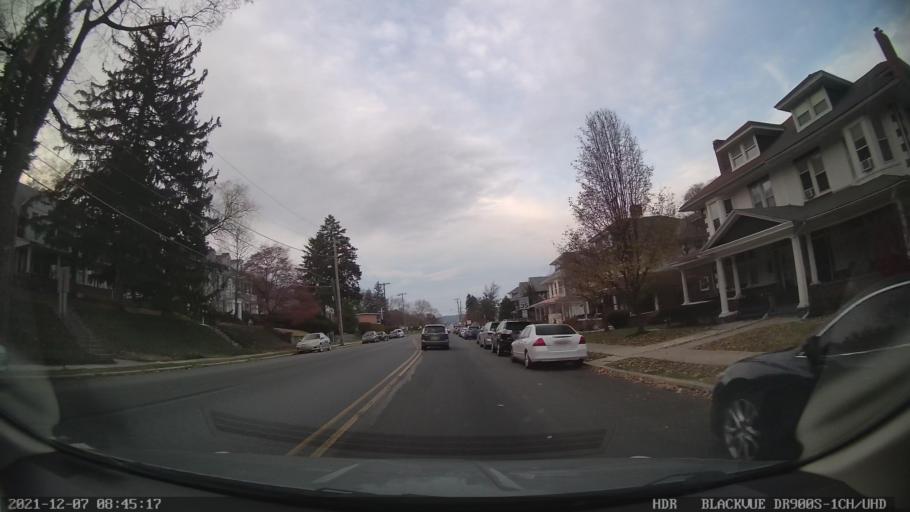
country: US
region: Pennsylvania
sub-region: Berks County
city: Hyde Park
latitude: 40.3558
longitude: -75.9084
